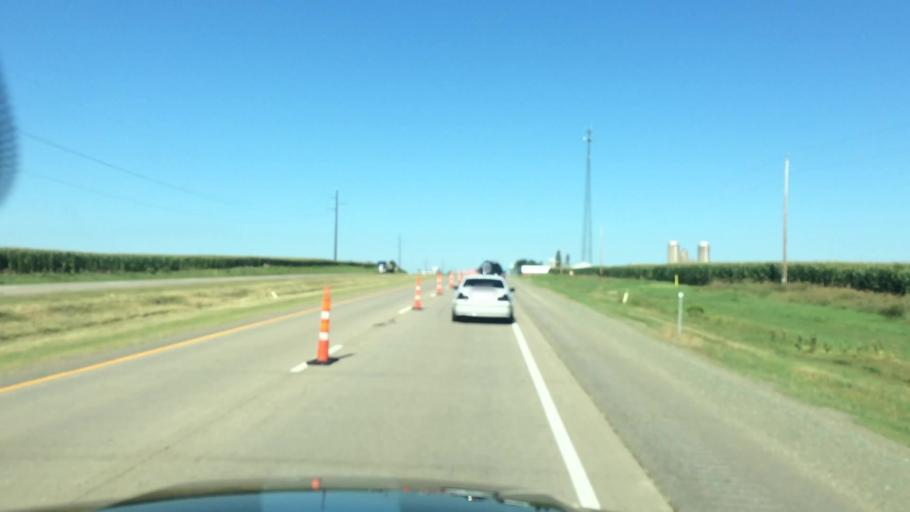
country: US
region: Wisconsin
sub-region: Marathon County
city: Marathon
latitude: 44.9446
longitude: -89.8986
